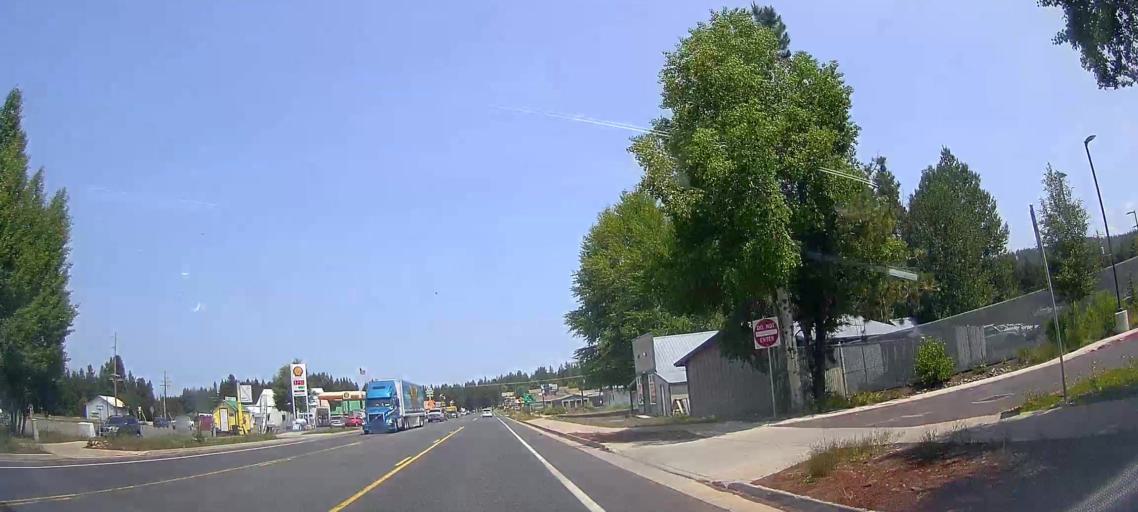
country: US
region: Oregon
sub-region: Deschutes County
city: La Pine
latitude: 43.4613
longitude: -121.6971
